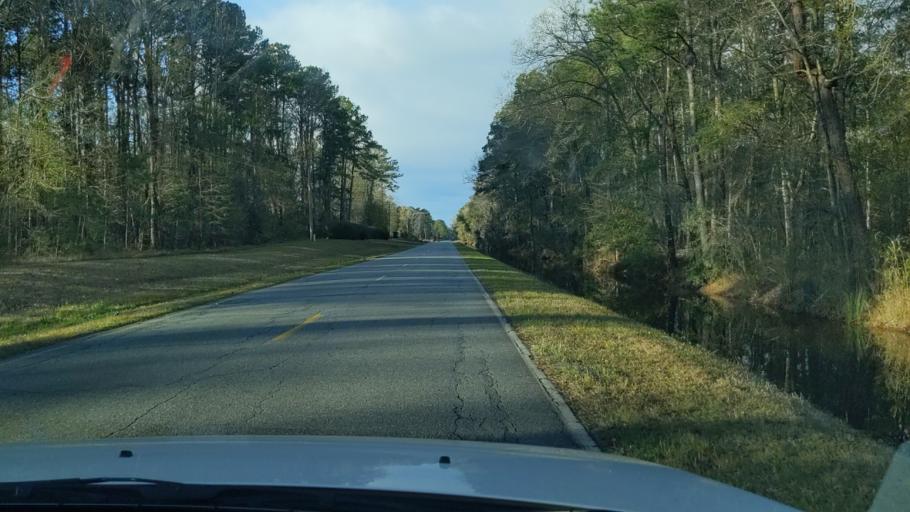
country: US
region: Georgia
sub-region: Chatham County
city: Pooler
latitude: 32.0411
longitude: -81.2972
